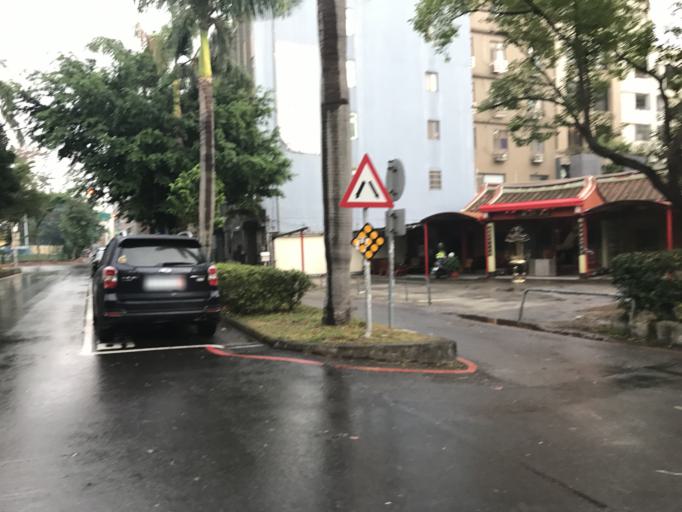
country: TW
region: Taiwan
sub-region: Hsinchu
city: Hsinchu
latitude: 24.8102
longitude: 120.9793
